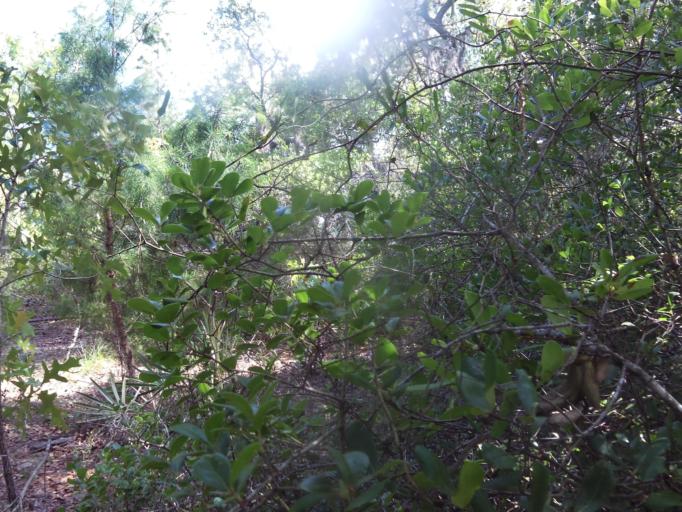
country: US
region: Florida
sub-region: Clay County
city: Keystone Heights
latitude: 29.8440
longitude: -81.9490
